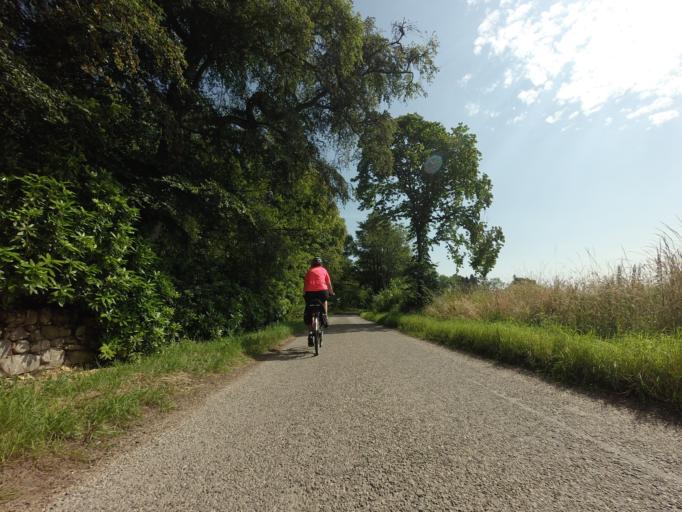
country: GB
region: Scotland
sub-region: Highland
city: Alness
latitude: 57.7208
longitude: -4.2103
